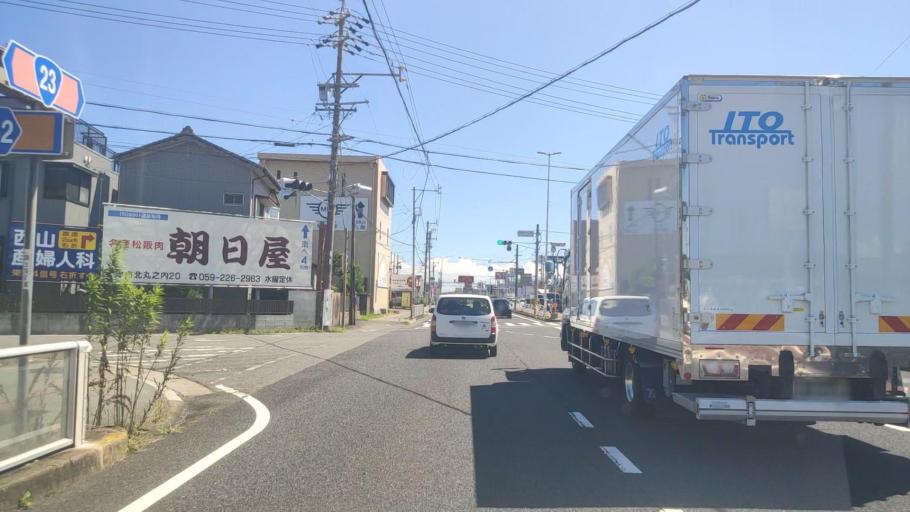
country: JP
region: Mie
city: Tsu-shi
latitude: 34.7562
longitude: 136.5232
